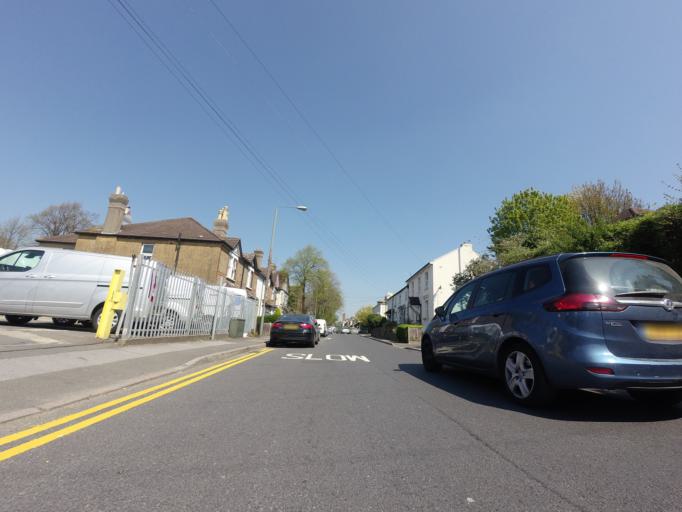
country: GB
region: England
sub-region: Greater London
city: Orpington
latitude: 51.3836
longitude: 0.1088
